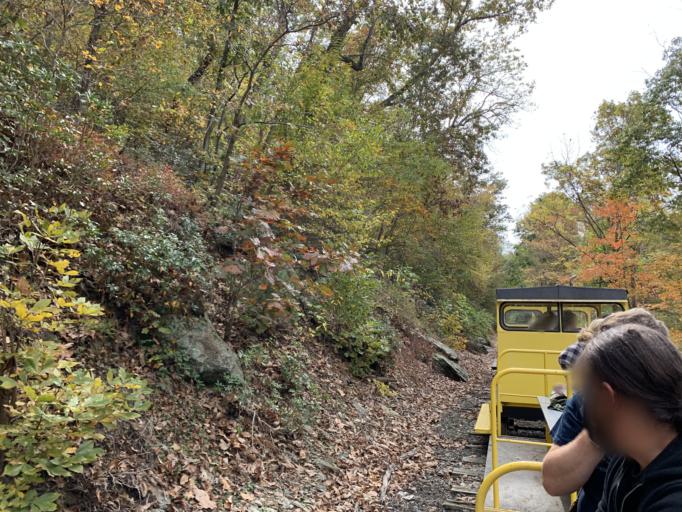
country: US
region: Pennsylvania
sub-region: York County
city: Susquehanna Trails
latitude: 39.8116
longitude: -76.4759
